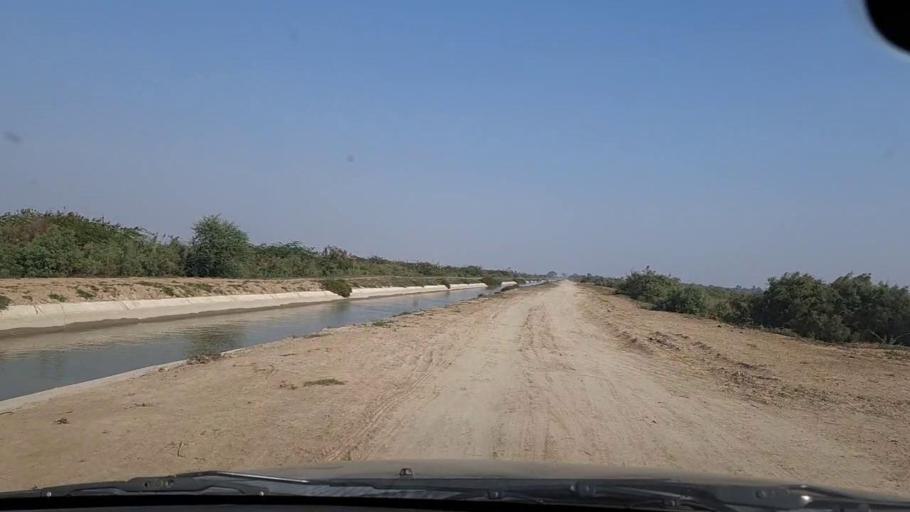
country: PK
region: Sindh
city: Mirpur Sakro
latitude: 24.3419
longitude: 67.7178
